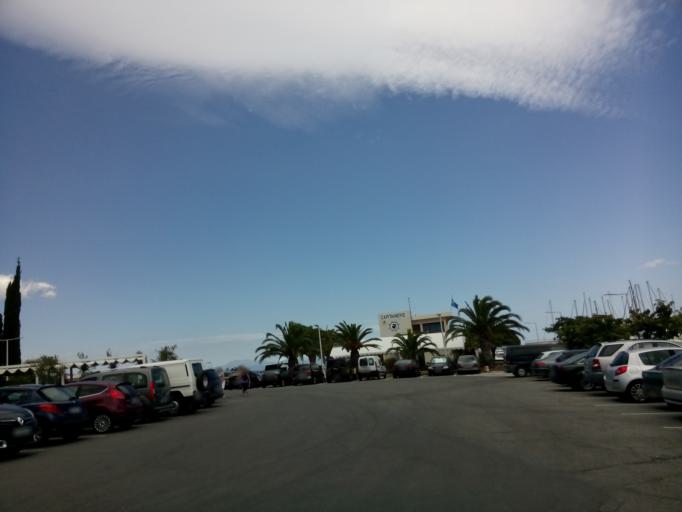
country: FR
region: Corsica
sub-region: Departement de la Corse-du-Sud
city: Sari-Solenzara
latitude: 41.8578
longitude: 9.4023
